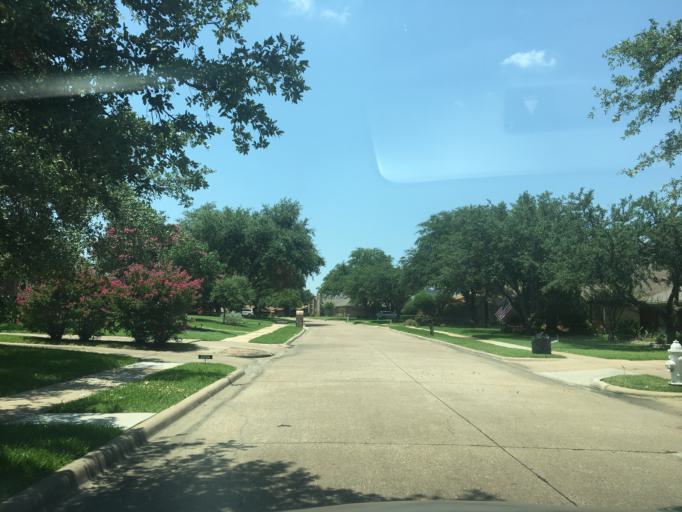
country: US
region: Texas
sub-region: Dallas County
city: Carrollton
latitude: 32.9475
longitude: -96.8625
